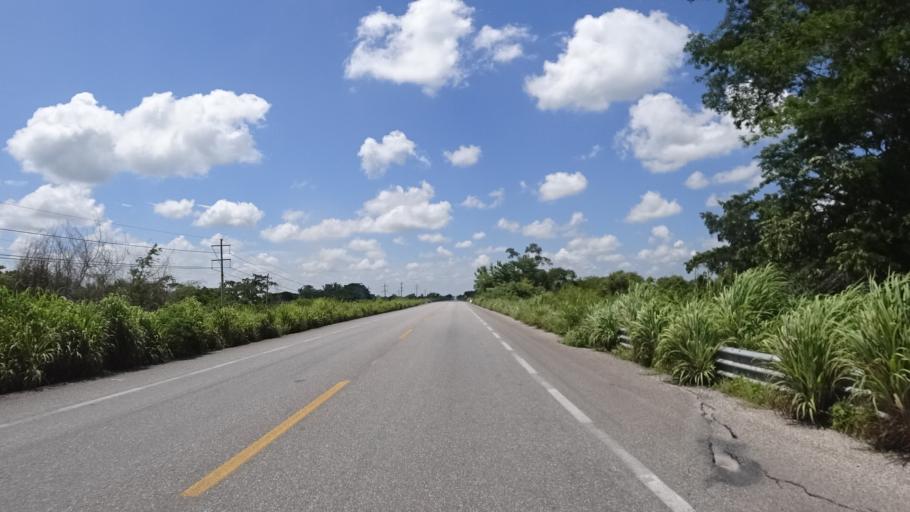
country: MX
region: Campeche
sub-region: Carmen
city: Licenciado Gustavo Diaz Ordaz (18 de Marzo)
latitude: 18.5695
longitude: -91.0546
